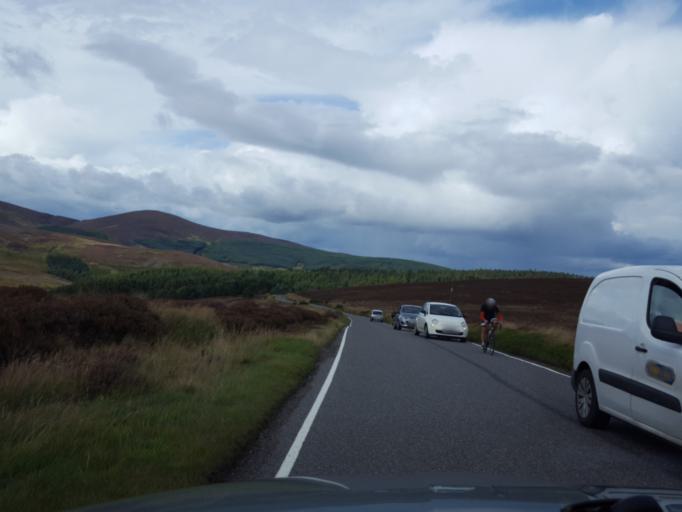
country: GB
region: Scotland
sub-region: Aberdeenshire
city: Banchory
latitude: 56.9416
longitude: -2.5750
